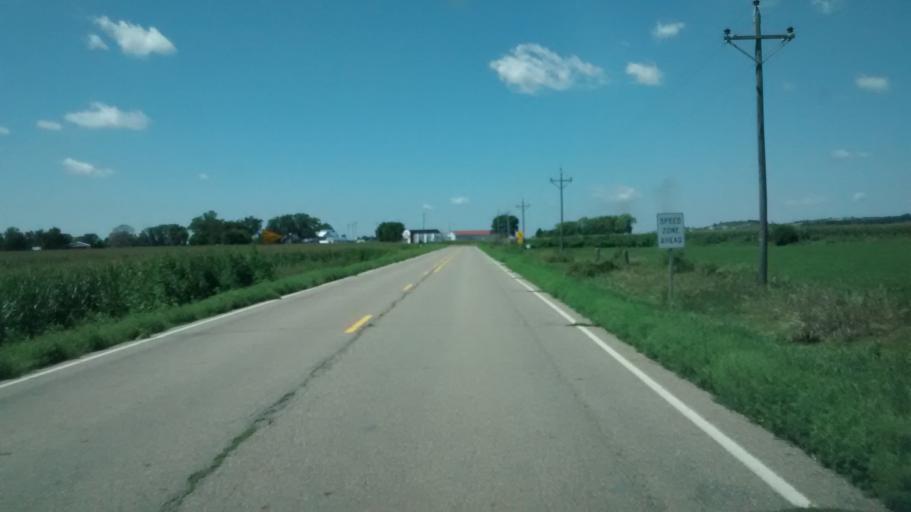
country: US
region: Iowa
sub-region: Woodbury County
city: Moville
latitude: 42.2699
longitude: -96.0719
